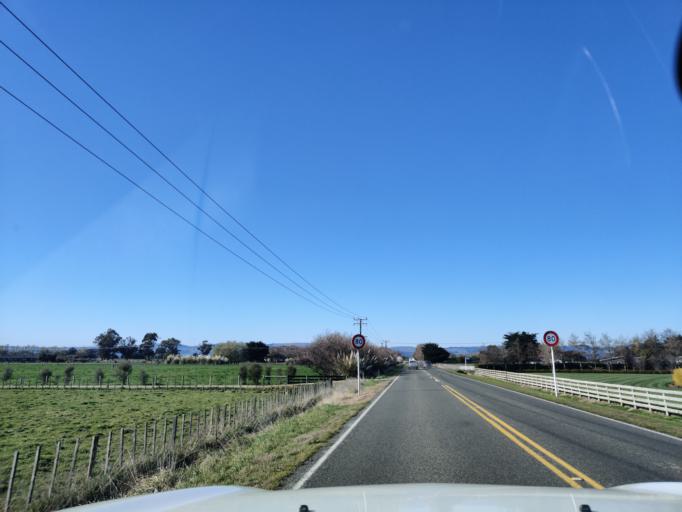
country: NZ
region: Manawatu-Wanganui
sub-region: Palmerston North City
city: Palmerston North
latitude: -40.3112
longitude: 175.5914
